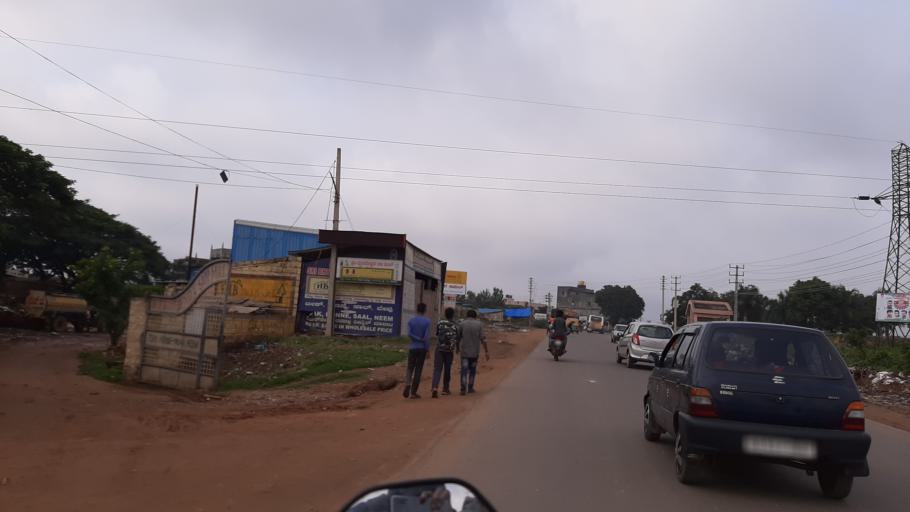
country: IN
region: Karnataka
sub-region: Bangalore Rural
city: Nelamangala
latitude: 12.9870
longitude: 77.4474
